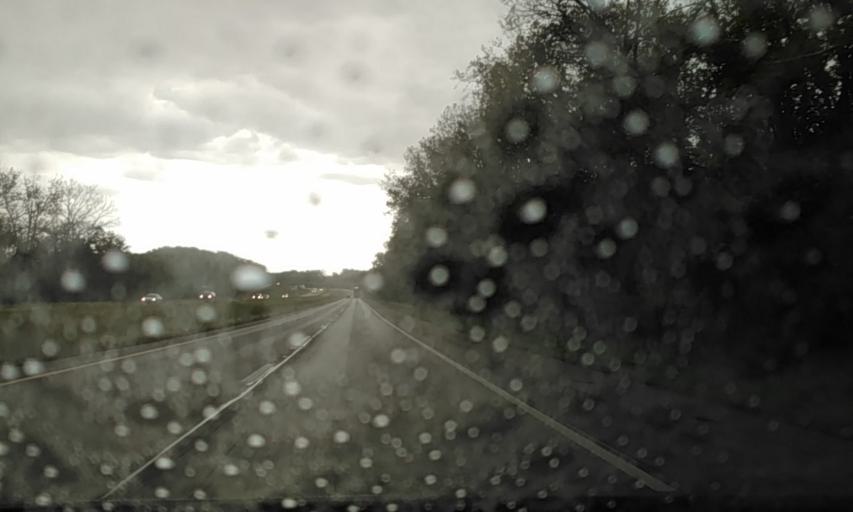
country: US
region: Illinois
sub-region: Bond County
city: Greenville
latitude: 38.8337
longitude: -89.5260
